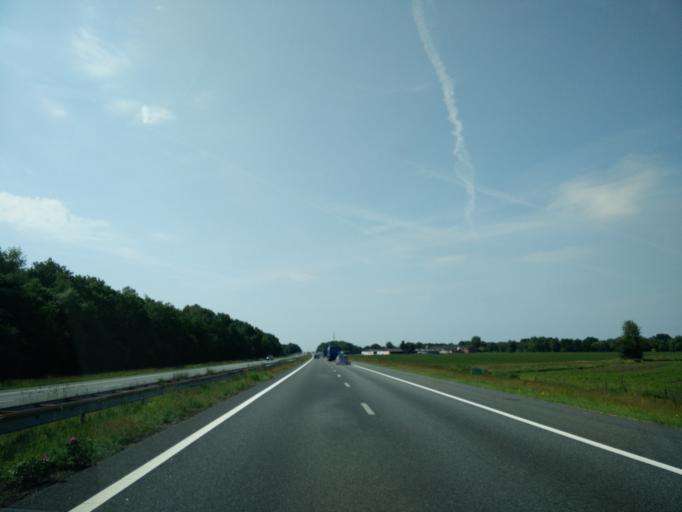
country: NL
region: Drenthe
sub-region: Gemeente Tynaarlo
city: Vries
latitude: 53.0545
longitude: 6.5957
